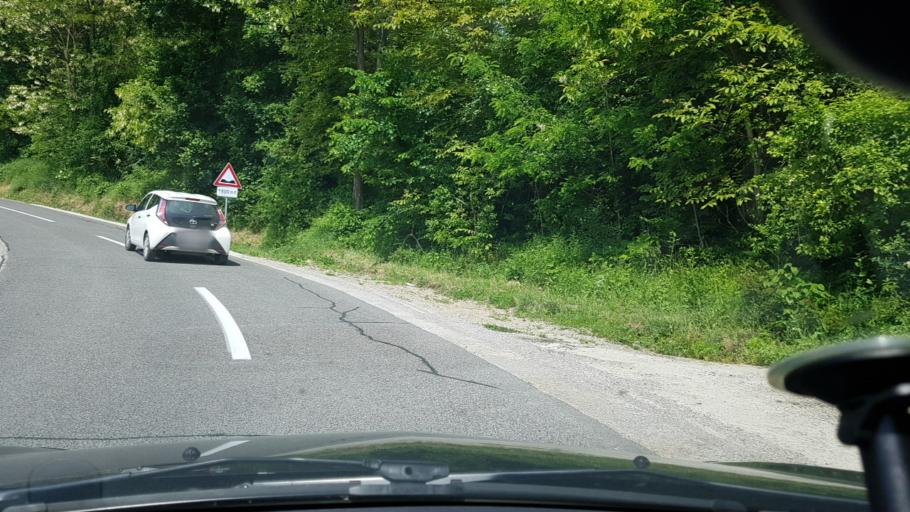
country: HR
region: Krapinsko-Zagorska
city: Marija Bistrica
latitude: 46.0094
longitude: 16.0934
